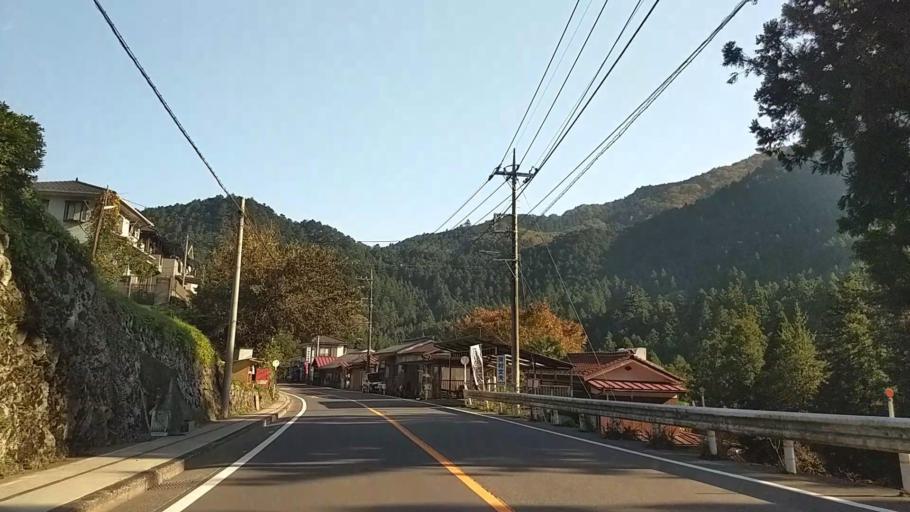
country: JP
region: Tokyo
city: Ome
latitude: 35.8098
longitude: 139.1586
